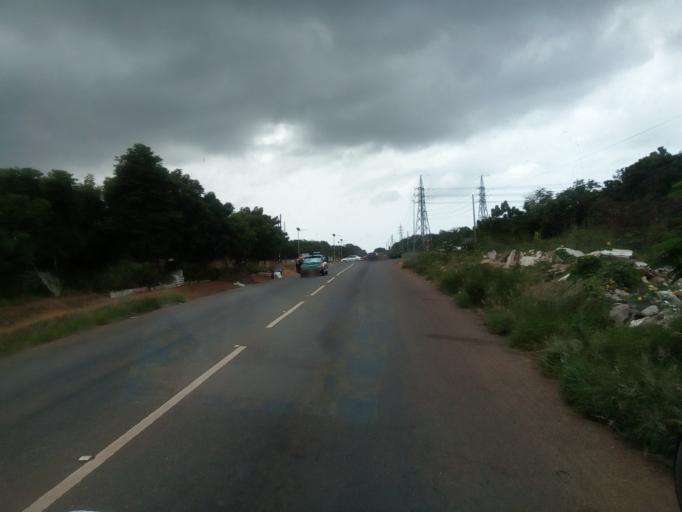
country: GH
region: Greater Accra
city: Dome
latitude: 5.6434
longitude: -0.2038
